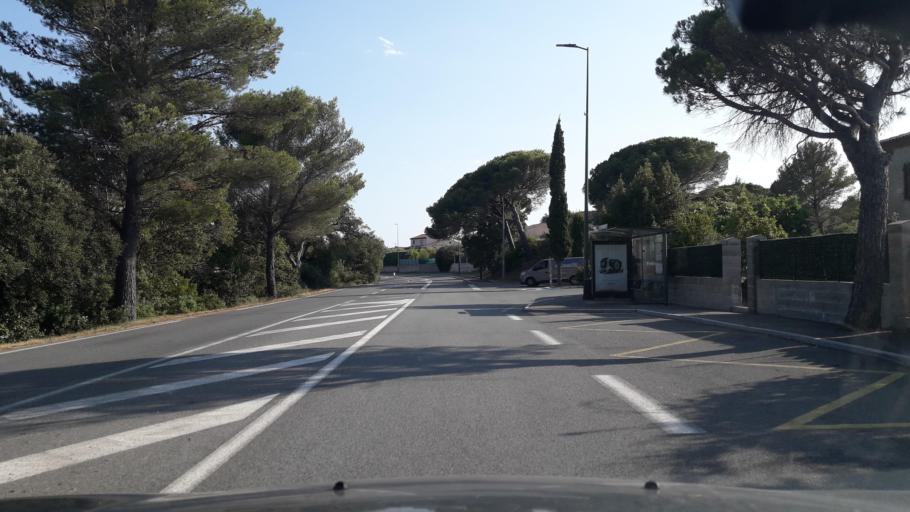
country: FR
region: Provence-Alpes-Cote d'Azur
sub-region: Departement du Var
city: Frejus
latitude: 43.4594
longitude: 6.7574
